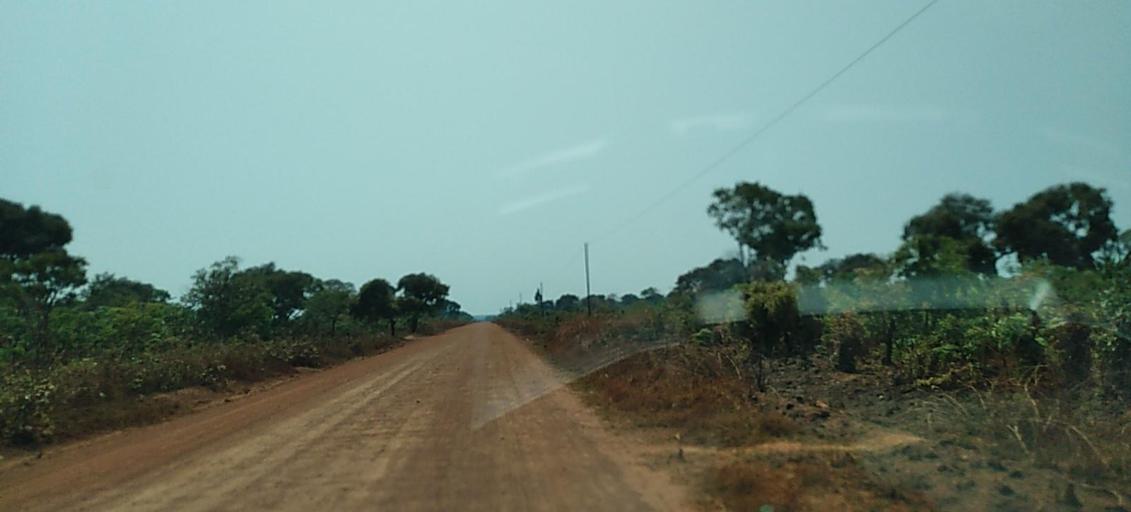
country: ZM
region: North-Western
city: Kansanshi
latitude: -11.9968
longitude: 26.6011
